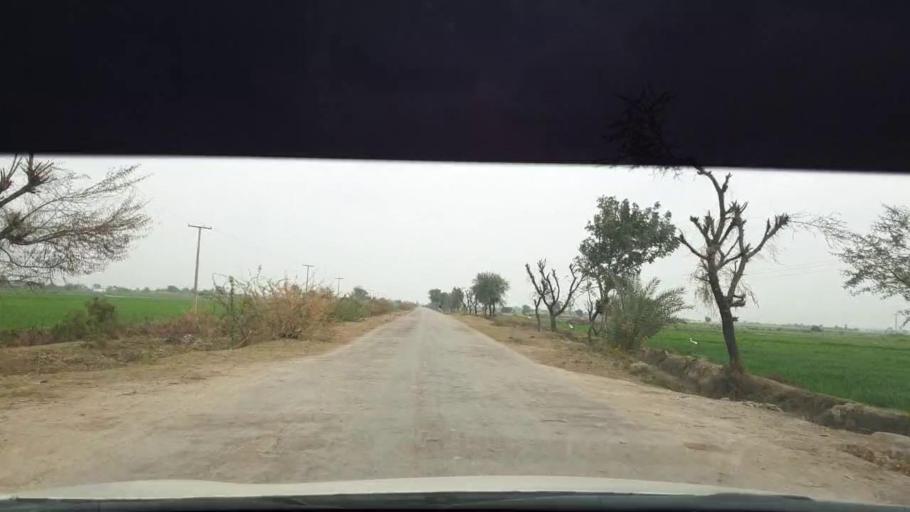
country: PK
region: Sindh
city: Berani
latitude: 25.7763
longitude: 68.8731
